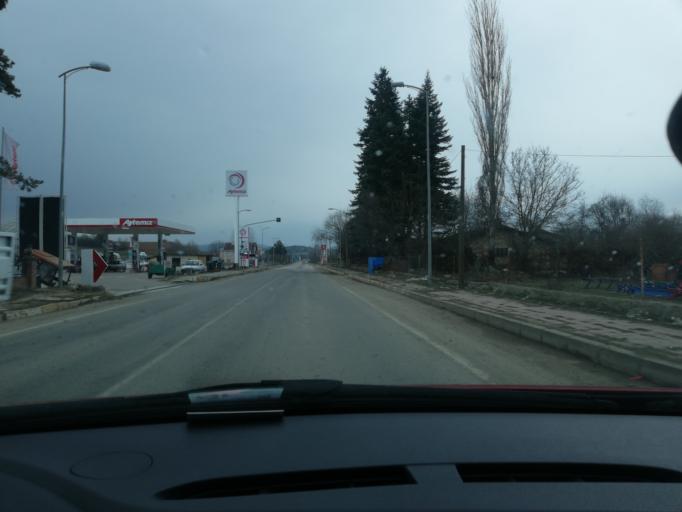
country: TR
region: Kastamonu
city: Daday
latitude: 41.4790
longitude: 33.4746
